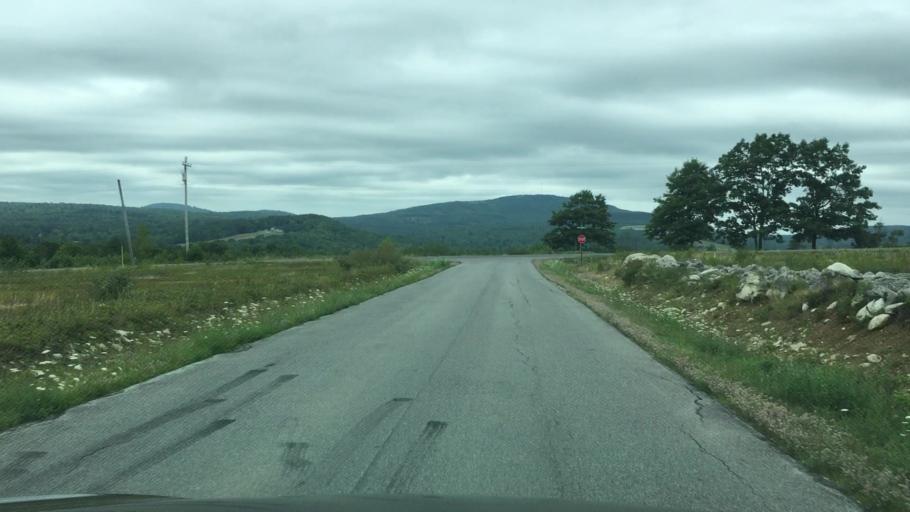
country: US
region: Maine
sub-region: Waldo County
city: Stockton Springs
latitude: 44.5249
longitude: -68.8818
